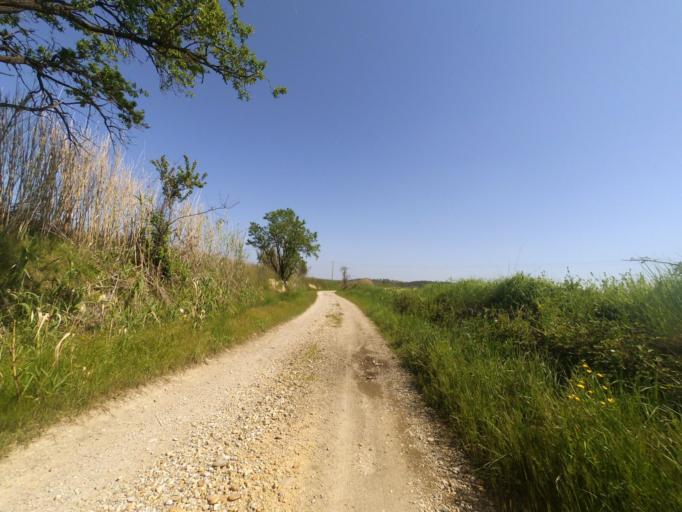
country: FR
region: Languedoc-Roussillon
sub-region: Departement du Gard
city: Congenies
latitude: 43.7734
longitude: 4.1707
